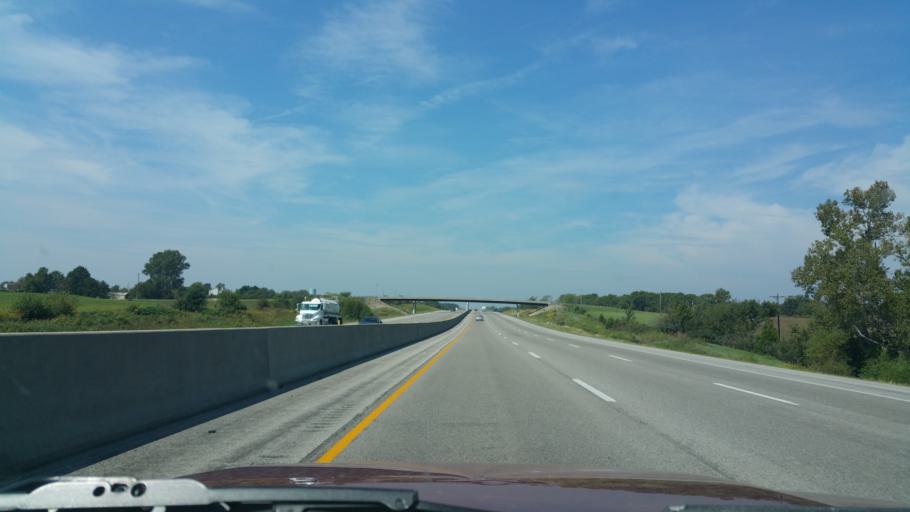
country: US
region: Kansas
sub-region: Douglas County
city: Lawrence
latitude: 39.0051
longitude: -95.4431
